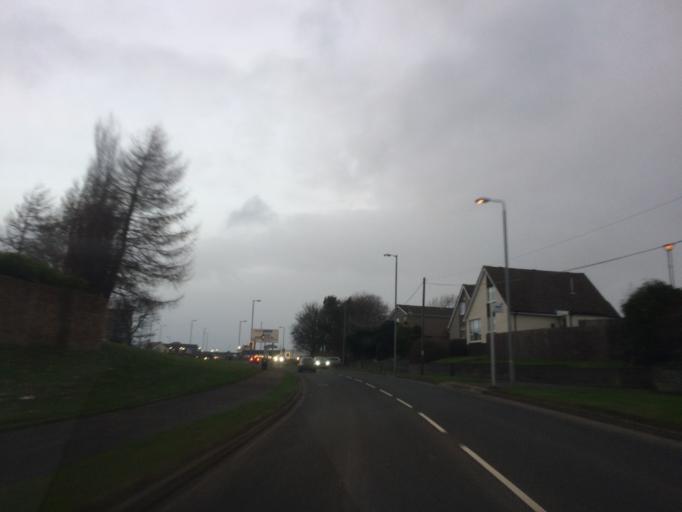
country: GB
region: Scotland
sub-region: East Renfrewshire
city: Newton Mearns
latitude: 55.7822
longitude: -4.3429
